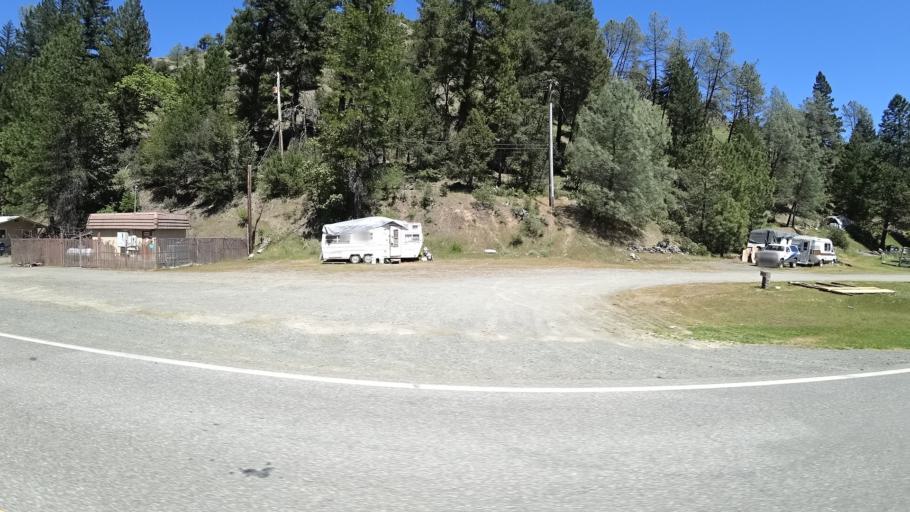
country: US
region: California
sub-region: Trinity County
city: Hayfork
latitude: 40.7432
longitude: -123.2673
